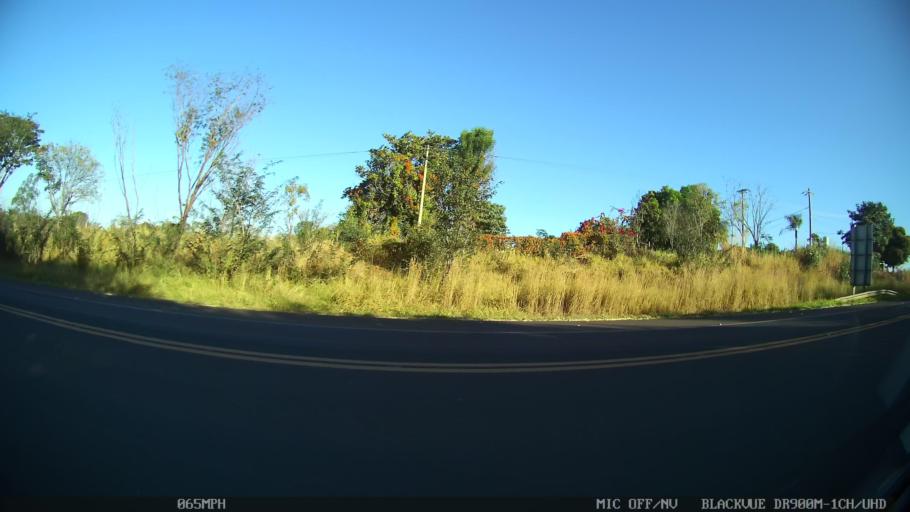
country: BR
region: Sao Paulo
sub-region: Guapiacu
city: Guapiacu
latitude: -20.7705
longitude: -49.2157
